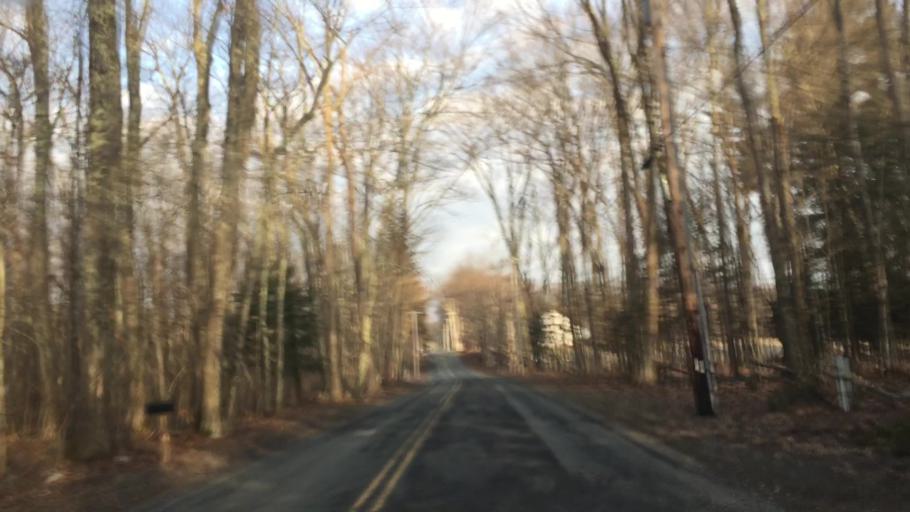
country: US
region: Massachusetts
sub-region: Berkshire County
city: New Marlborough
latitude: 42.1567
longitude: -73.2671
